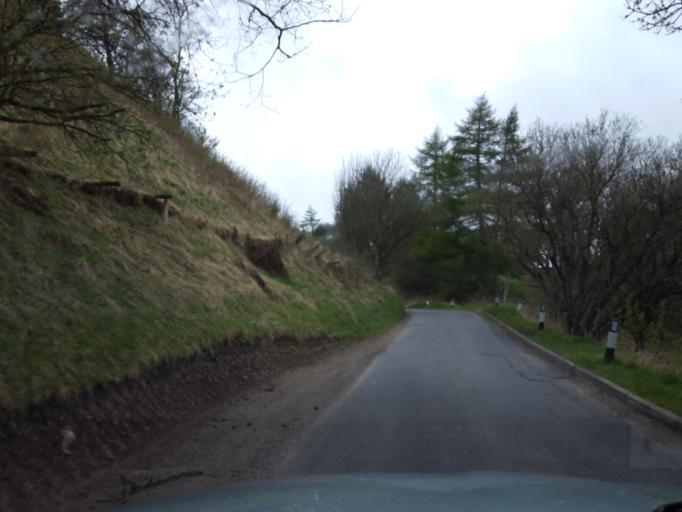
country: GB
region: Scotland
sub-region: Perth and Kinross
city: Errol
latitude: 56.4349
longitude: -3.2879
